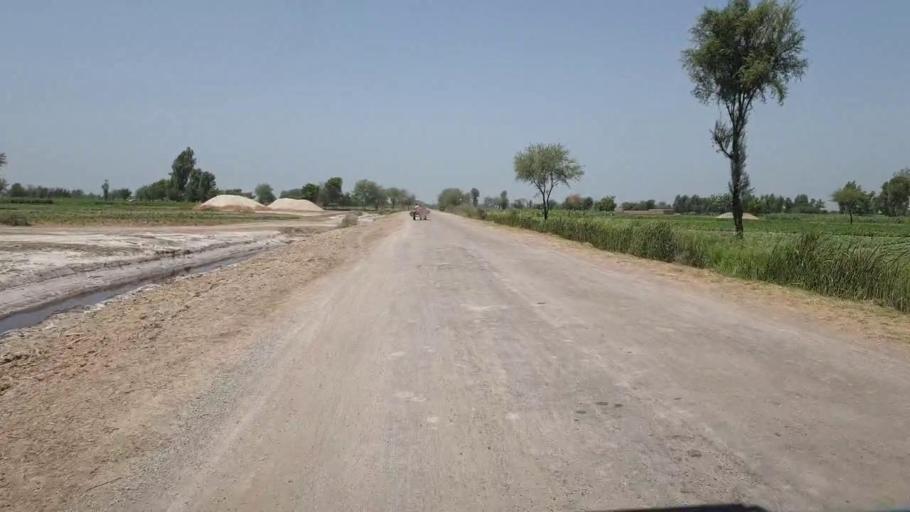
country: PK
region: Sindh
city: Nawabshah
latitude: 26.3556
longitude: 68.3992
